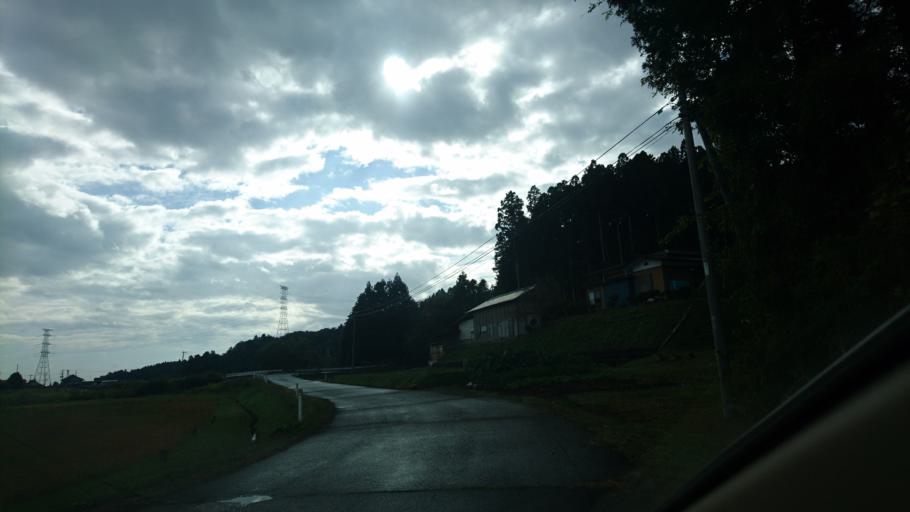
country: JP
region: Iwate
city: Ichinoseki
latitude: 38.7954
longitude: 140.9900
